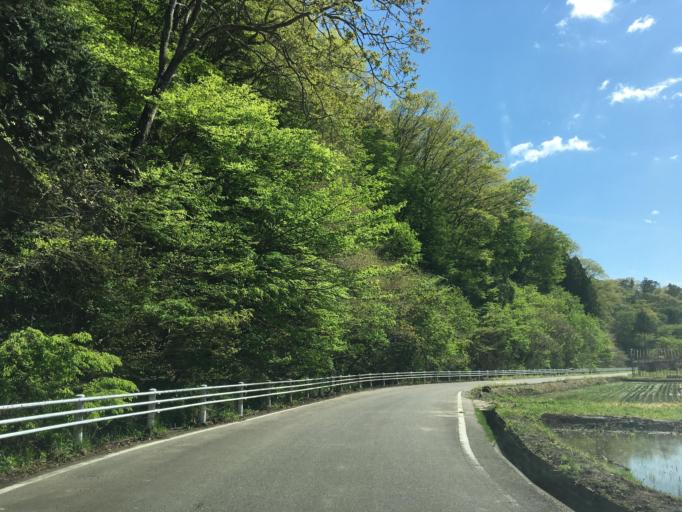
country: JP
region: Fukushima
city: Funehikimachi-funehiki
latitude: 37.3006
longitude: 140.6645
